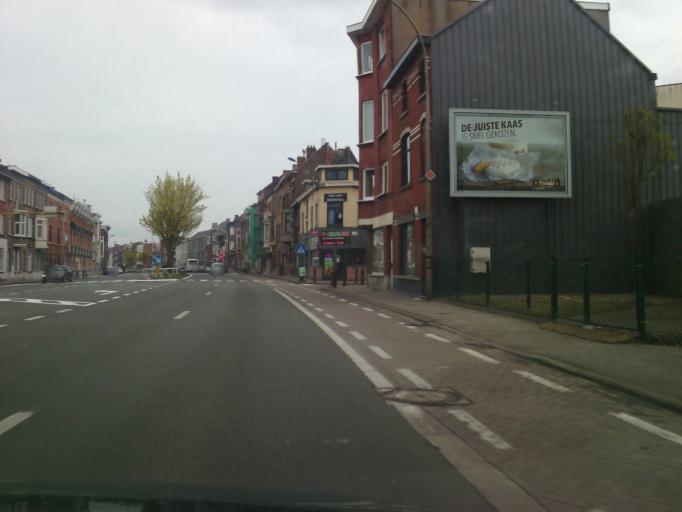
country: BE
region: Flanders
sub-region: Provincie Oost-Vlaanderen
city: Gent
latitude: 51.0616
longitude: 3.6936
